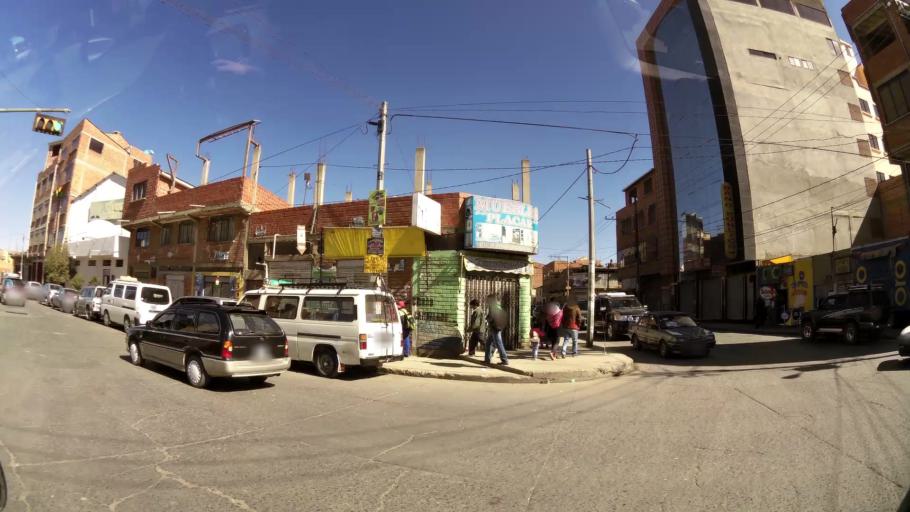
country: BO
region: La Paz
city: La Paz
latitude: -16.5154
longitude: -68.1633
